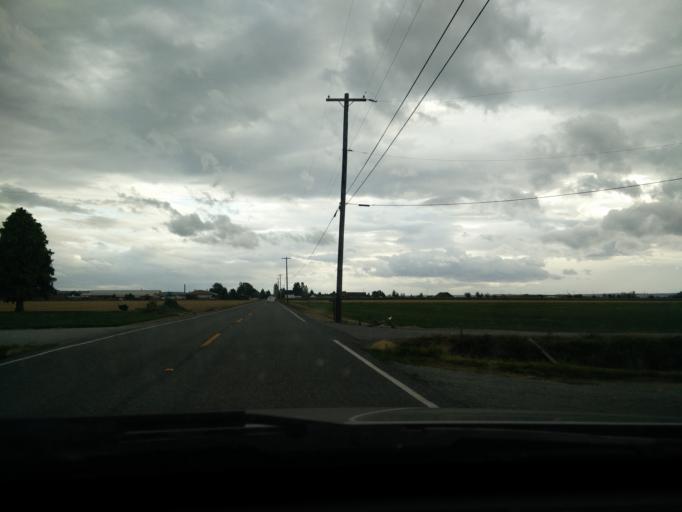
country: US
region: Washington
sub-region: Snohomish County
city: Stanwood
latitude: 48.2560
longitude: -122.3708
